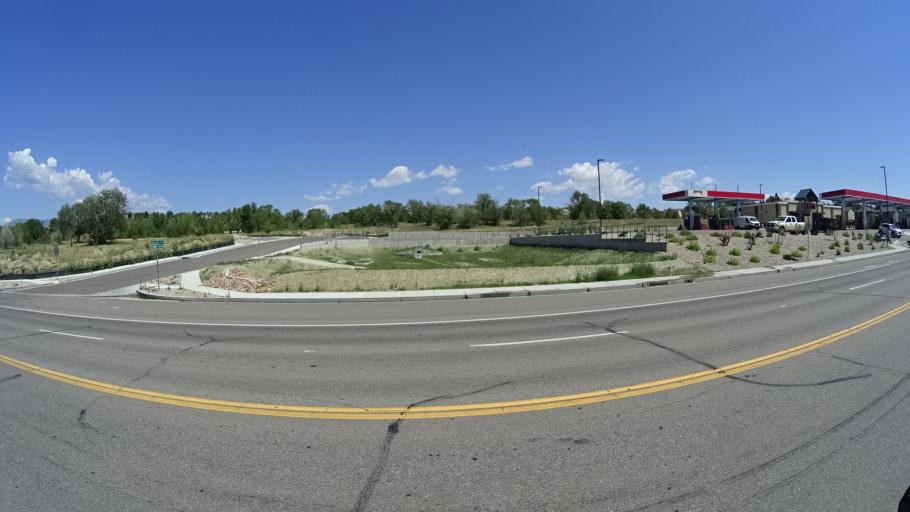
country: US
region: Colorado
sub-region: El Paso County
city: Stratmoor
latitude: 38.7970
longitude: -104.7792
